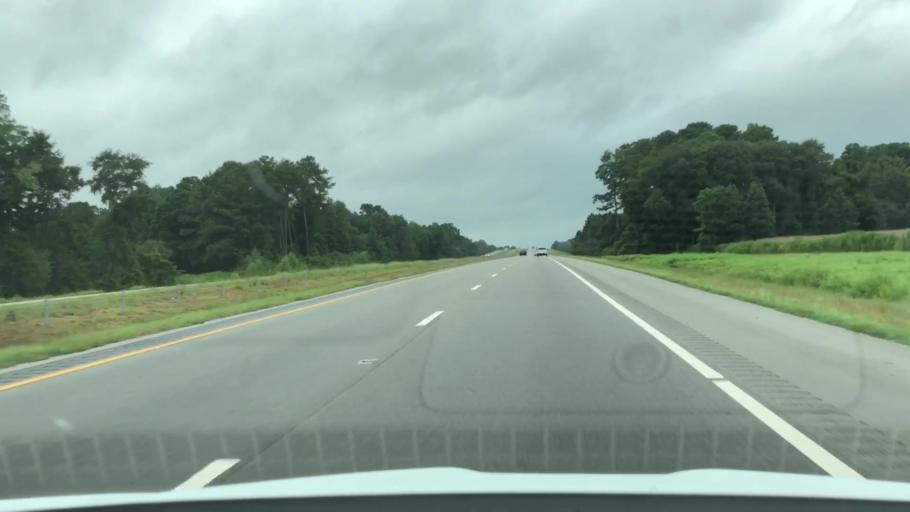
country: US
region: North Carolina
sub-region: Lenoir County
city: La Grange
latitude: 35.3351
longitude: -77.8434
